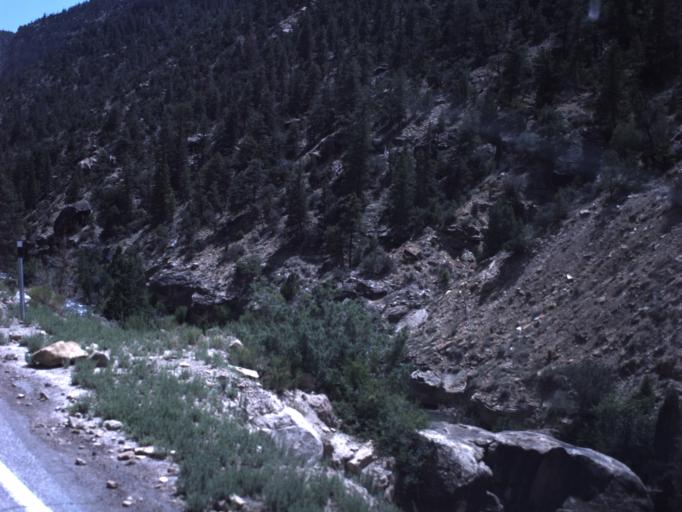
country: US
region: Utah
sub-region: Emery County
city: Orangeville
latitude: 39.2841
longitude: -111.2349
